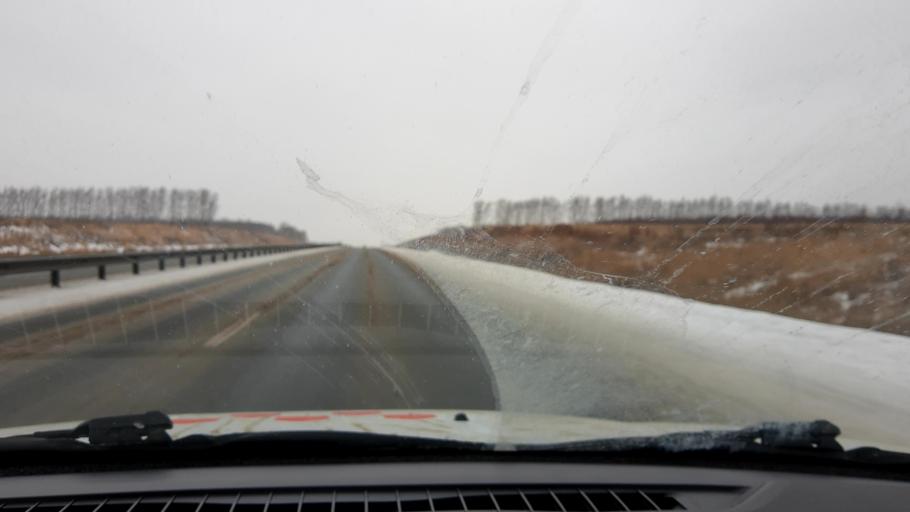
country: RU
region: Nizjnij Novgorod
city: Afonino
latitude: 56.1032
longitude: 44.0115
